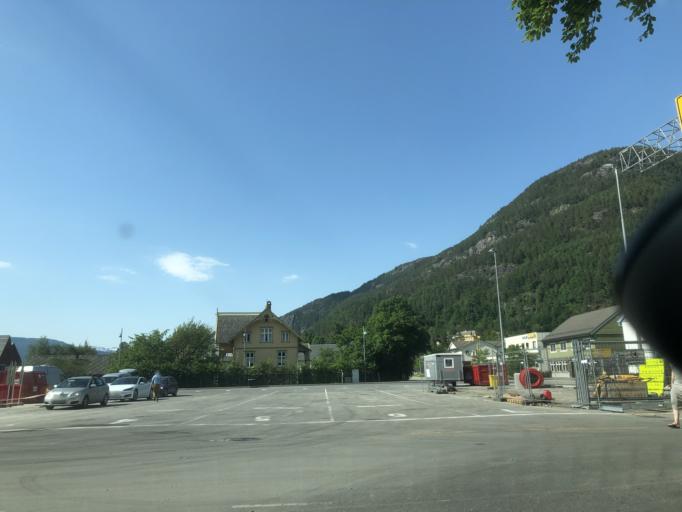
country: NO
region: Hordaland
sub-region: Jondal
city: Jondal
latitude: 60.2756
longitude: 6.2520
